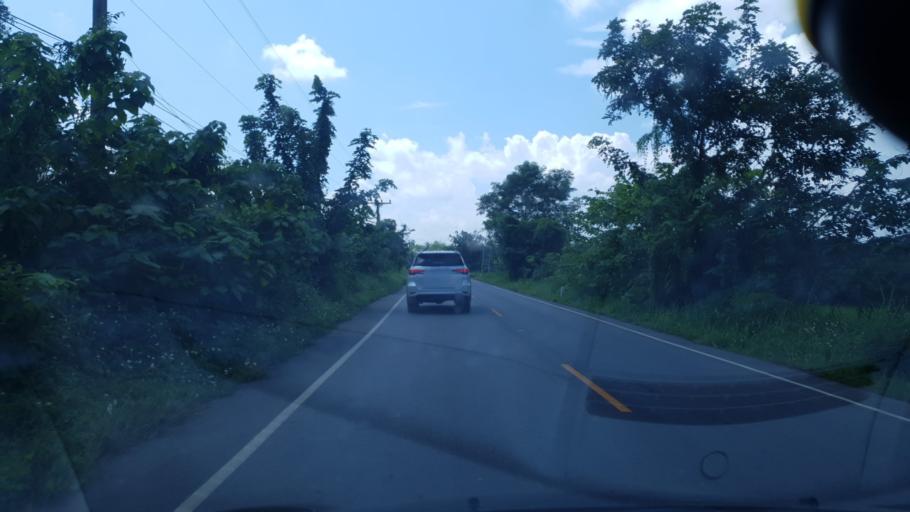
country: TH
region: Chiang Rai
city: Wiang Chai
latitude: 19.9225
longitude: 99.8967
